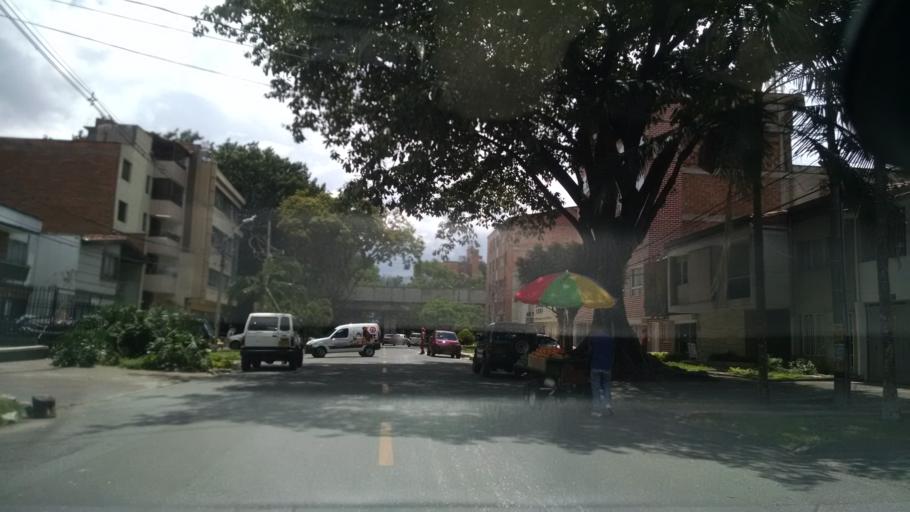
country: CO
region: Antioquia
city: Medellin
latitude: 6.2591
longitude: -75.5947
